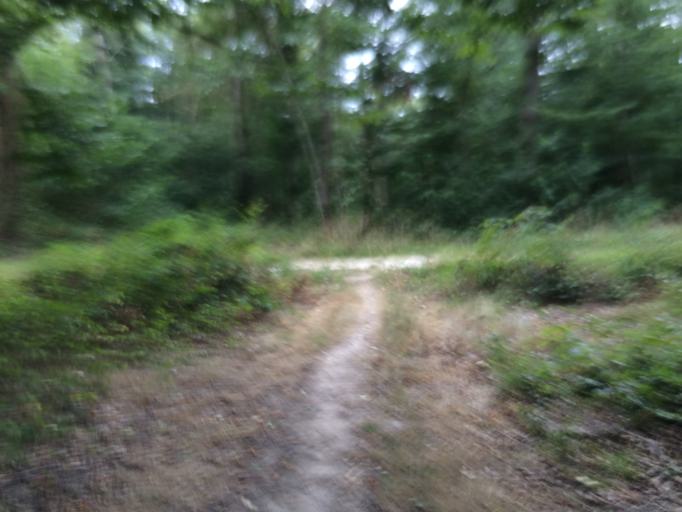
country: FR
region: Ile-de-France
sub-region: Departement de l'Essonne
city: Quincy-sous-Senart
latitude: 48.6523
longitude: 2.5357
